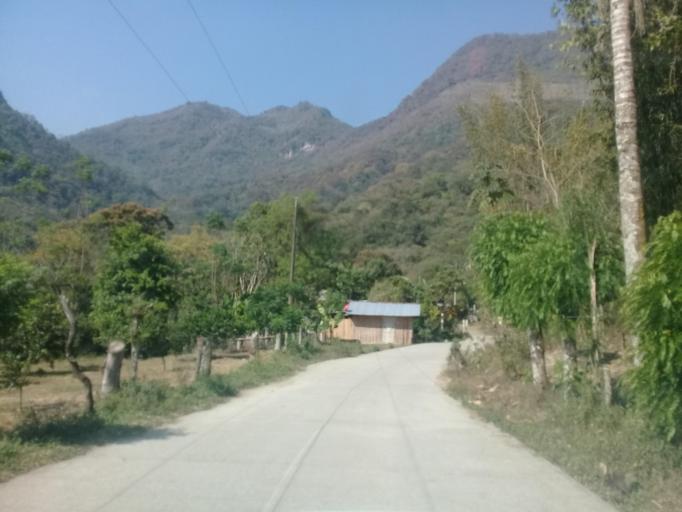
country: MX
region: Veracruz
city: Rafael Delgado
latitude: 18.7803
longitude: -97.0215
